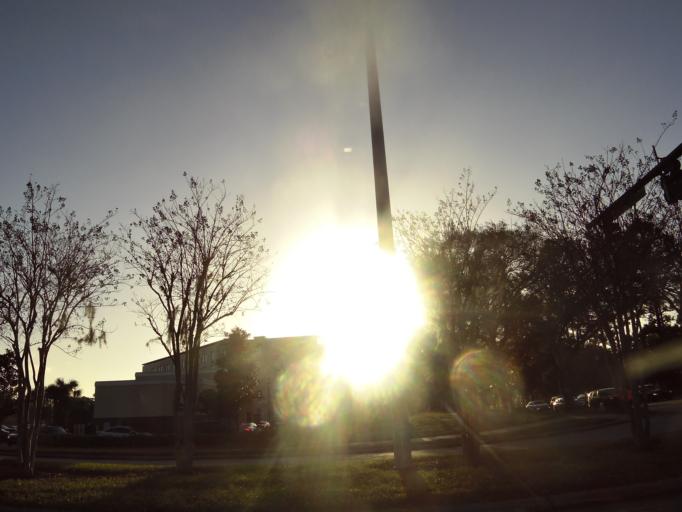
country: US
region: Florida
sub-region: Duval County
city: Jacksonville
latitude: 30.2606
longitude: -81.5539
